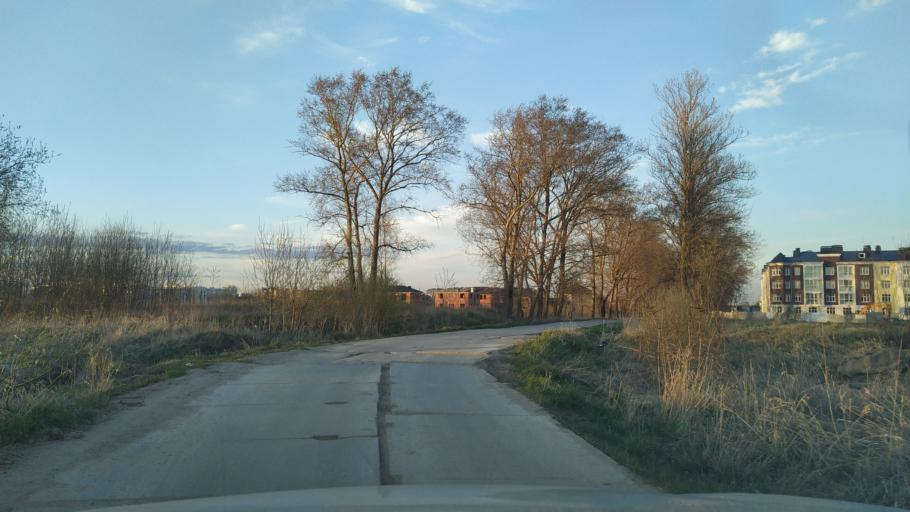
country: RU
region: St.-Petersburg
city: Pushkin
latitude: 59.6903
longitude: 30.4058
